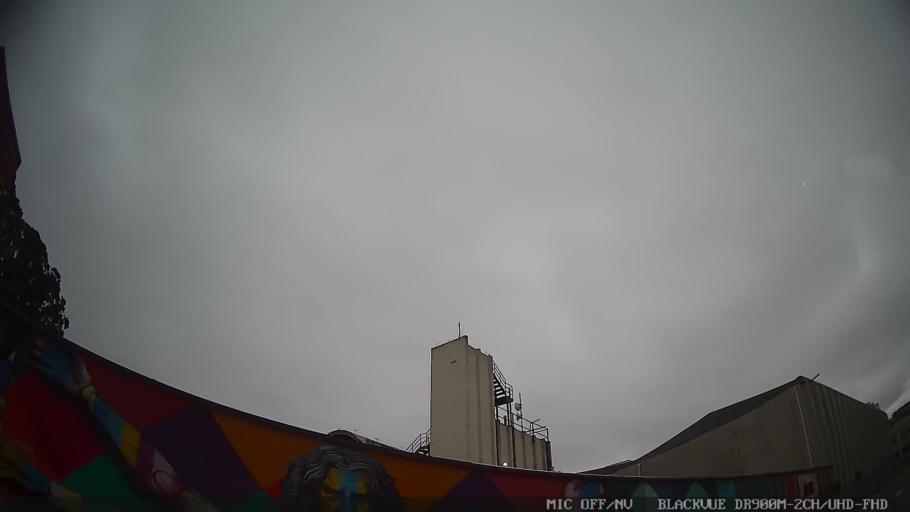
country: BR
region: Sao Paulo
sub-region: Sao Paulo
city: Sao Paulo
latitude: -23.5131
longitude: -46.6941
